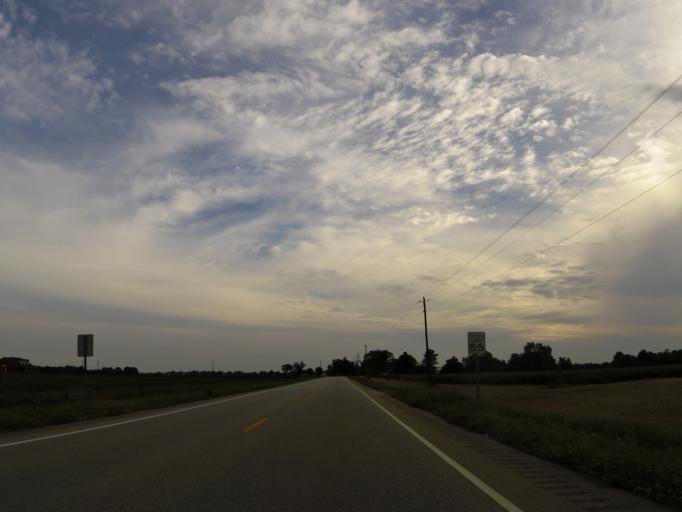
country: US
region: Alabama
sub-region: Monroe County
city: Frisco City
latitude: 31.2958
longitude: -87.5044
